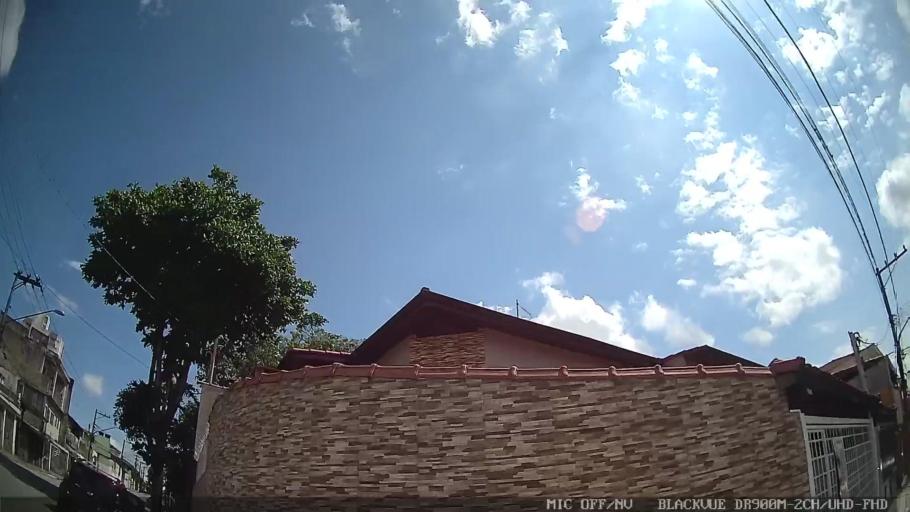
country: BR
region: Sao Paulo
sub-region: Guarulhos
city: Guarulhos
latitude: -23.5050
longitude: -46.4876
